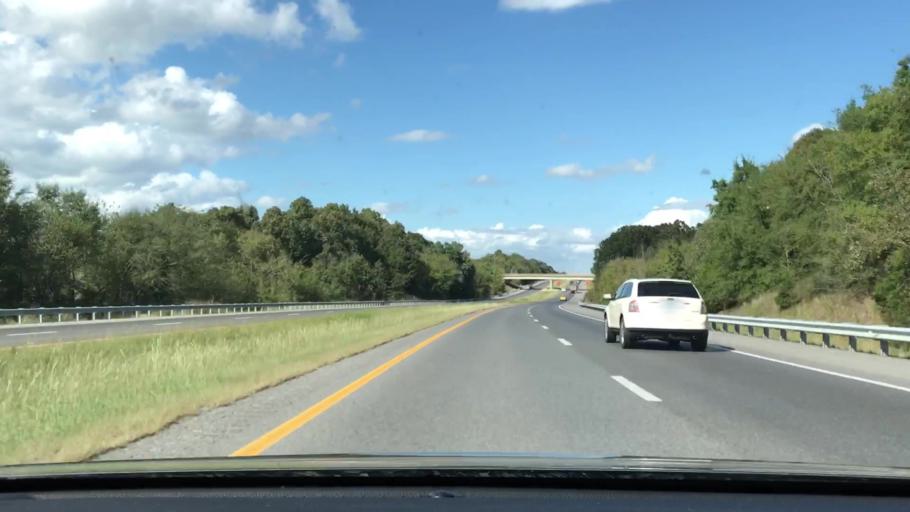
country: US
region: Kentucky
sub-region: Marshall County
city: Calvert City
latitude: 36.9520
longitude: -88.3500
